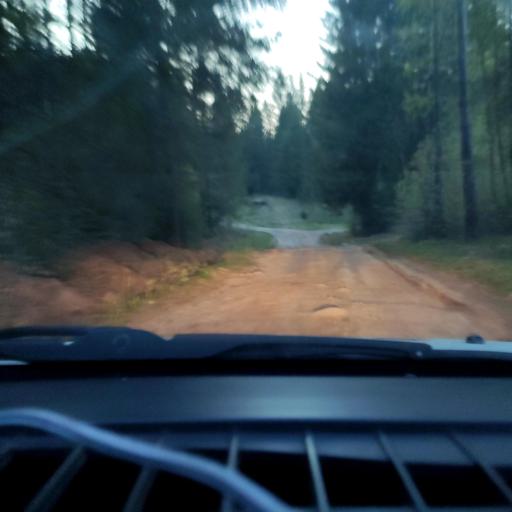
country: RU
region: Perm
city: Perm
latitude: 58.1537
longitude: 56.2917
